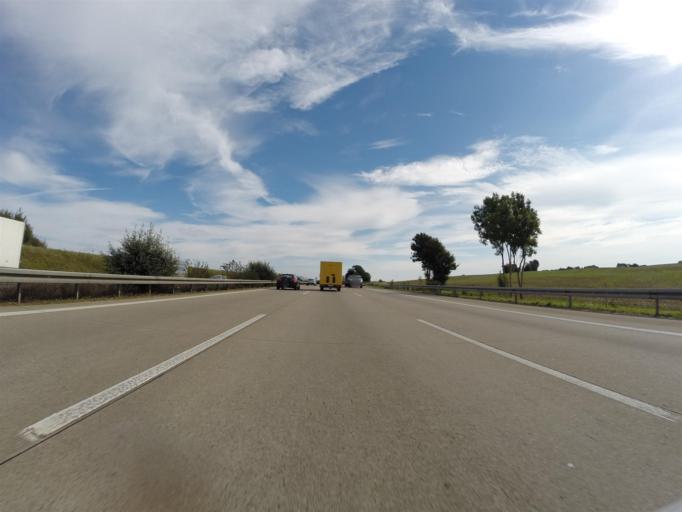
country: DE
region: Saxony
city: Klipphausen
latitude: 51.0606
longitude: 13.4542
